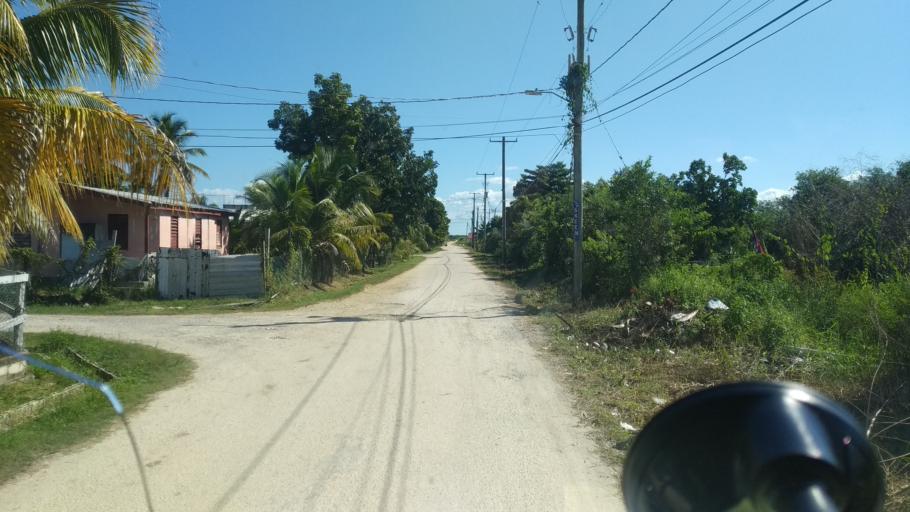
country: BZ
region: Belize
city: Belize City
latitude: 17.5610
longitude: -88.3022
